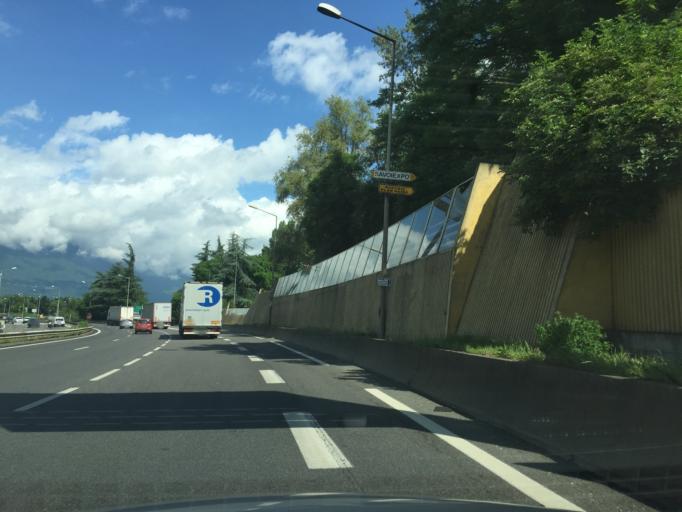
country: FR
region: Rhone-Alpes
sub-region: Departement de la Savoie
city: Cognin
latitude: 45.5833
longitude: 5.9112
